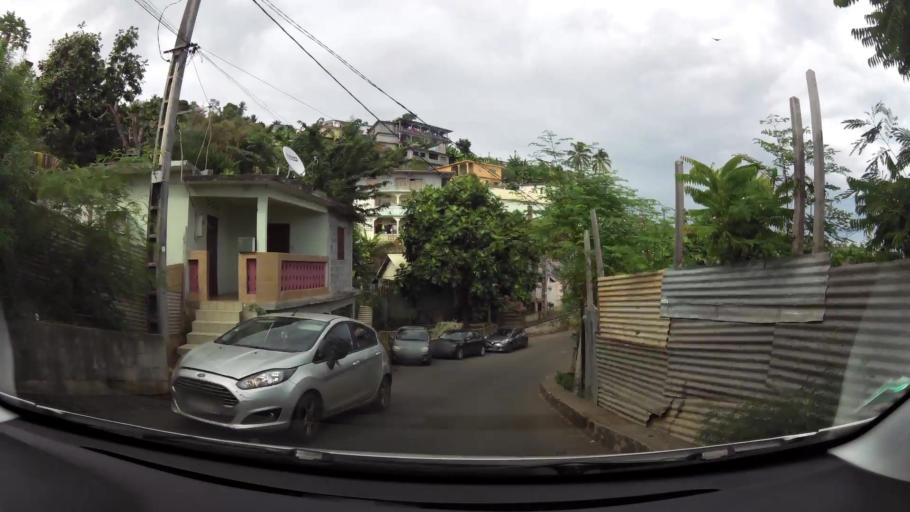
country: YT
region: Sada
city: Sada
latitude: -12.8484
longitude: 45.1013
